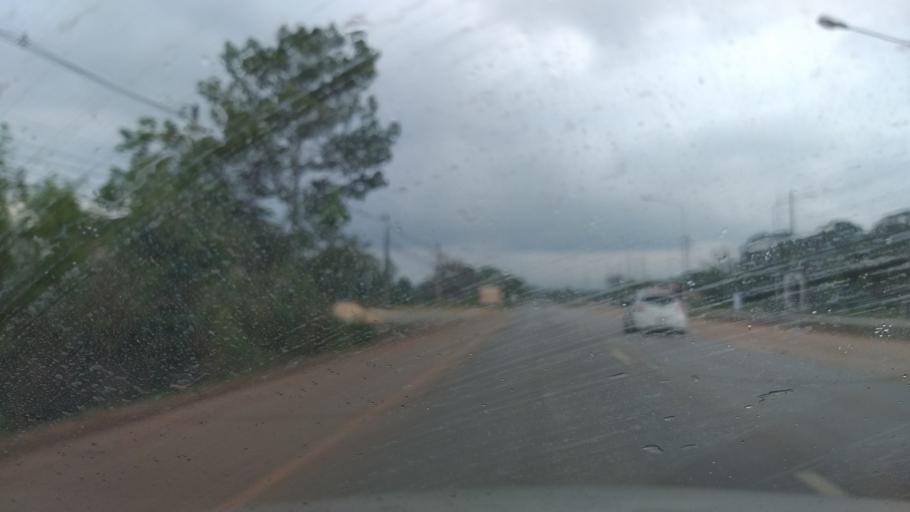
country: TH
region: Chanthaburi
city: Khlung
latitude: 12.4460
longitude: 102.2922
